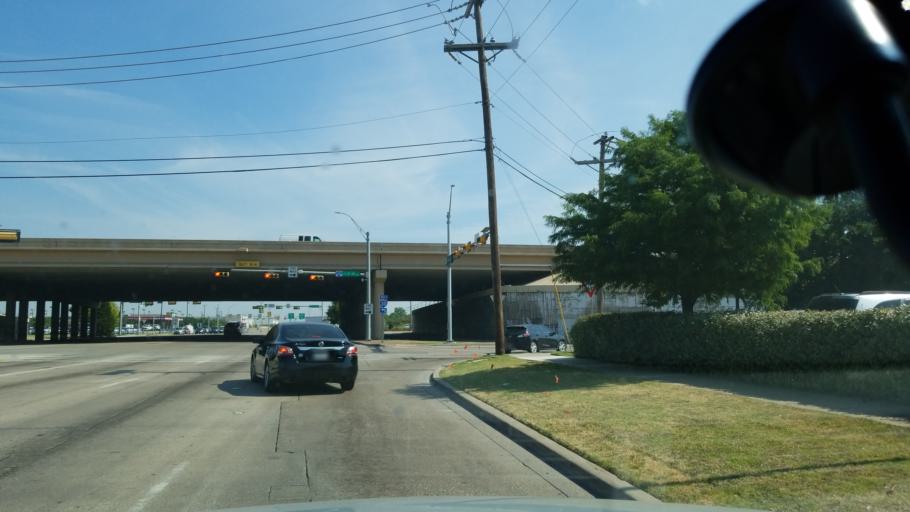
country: US
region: Texas
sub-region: Dallas County
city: Grand Prairie
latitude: 32.7578
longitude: -96.9948
